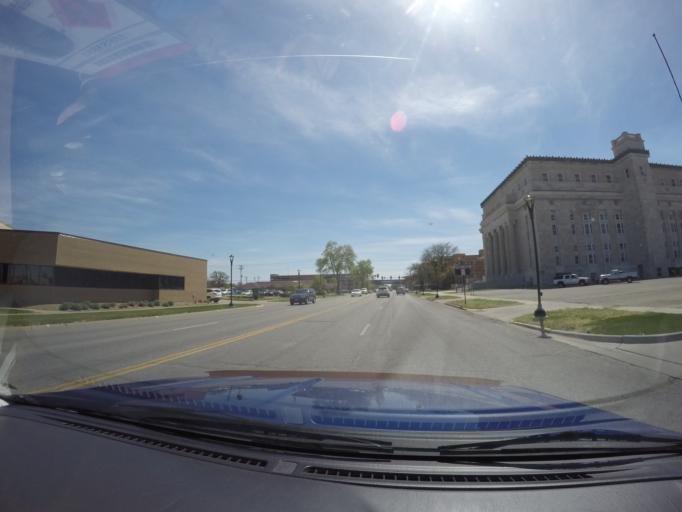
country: US
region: Kansas
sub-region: Saline County
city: Salina
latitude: 38.8353
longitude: -97.6092
